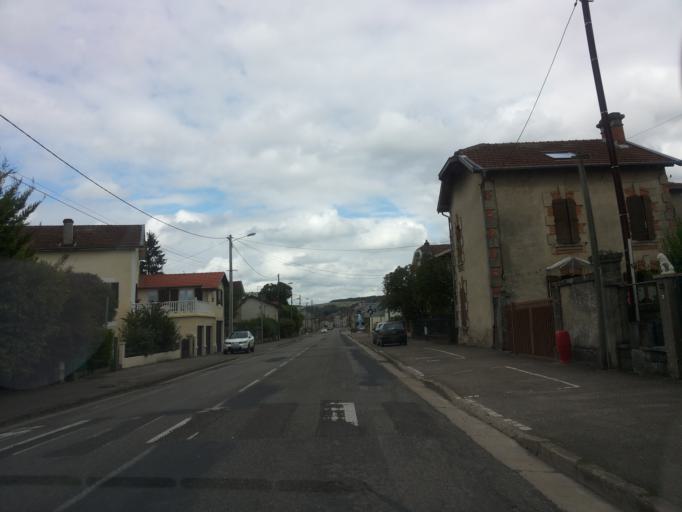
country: FR
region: Lorraine
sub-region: Departement de la Meuse
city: Ligny-en-Barrois
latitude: 48.6817
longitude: 5.3253
